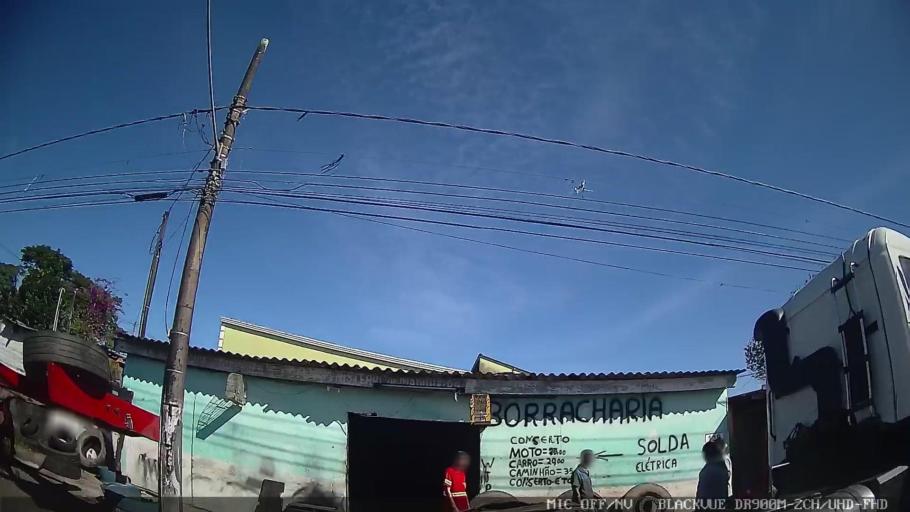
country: BR
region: Sao Paulo
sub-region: Santos
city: Santos
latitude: -23.9400
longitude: -46.2909
